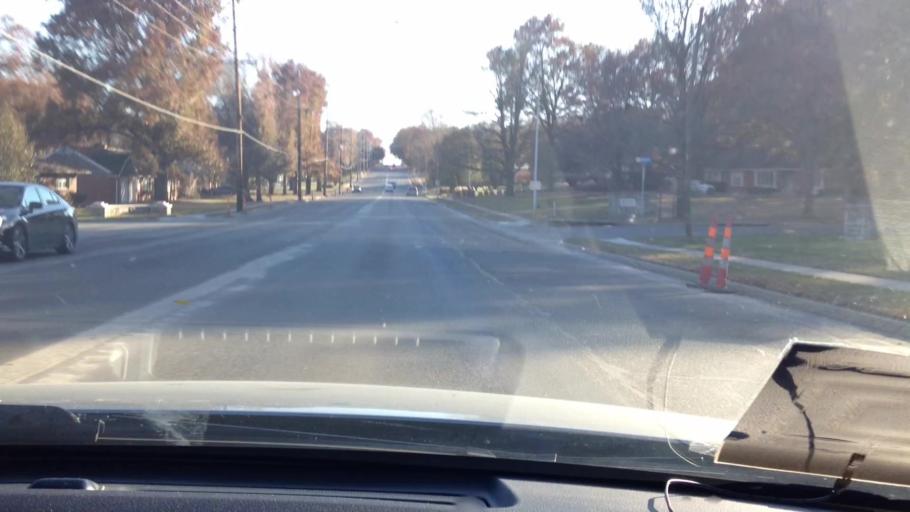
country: US
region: Kansas
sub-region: Johnson County
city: Leawood
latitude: 38.9681
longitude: -94.6304
